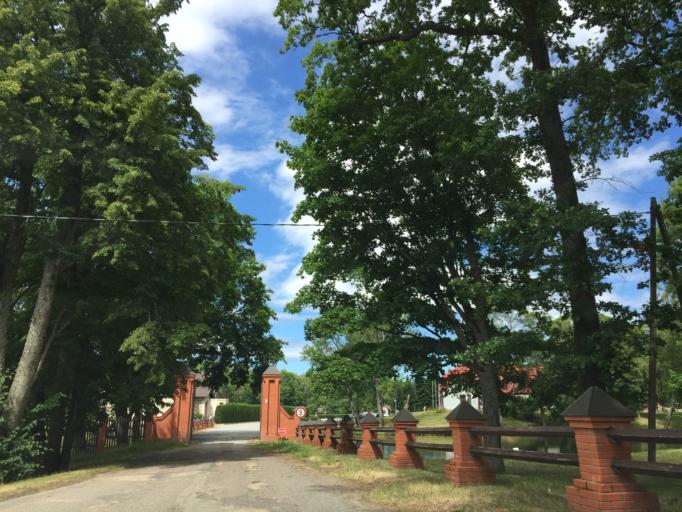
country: LV
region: Saulkrastu
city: Saulkrasti
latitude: 57.4035
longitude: 24.4256
